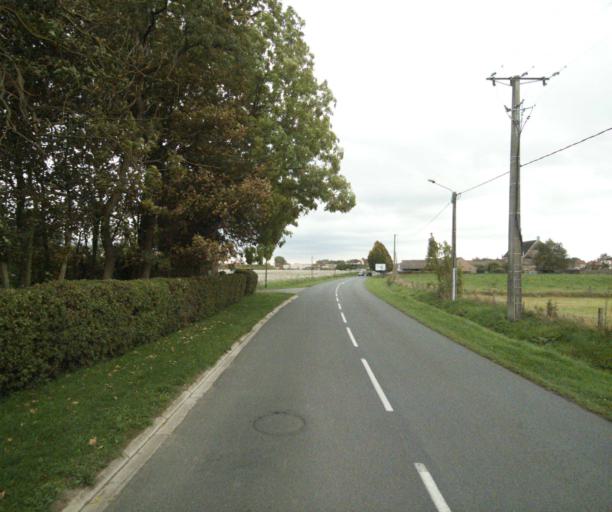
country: FR
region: Nord-Pas-de-Calais
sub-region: Departement du Nord
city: Marquillies
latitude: 50.5609
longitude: 2.8687
